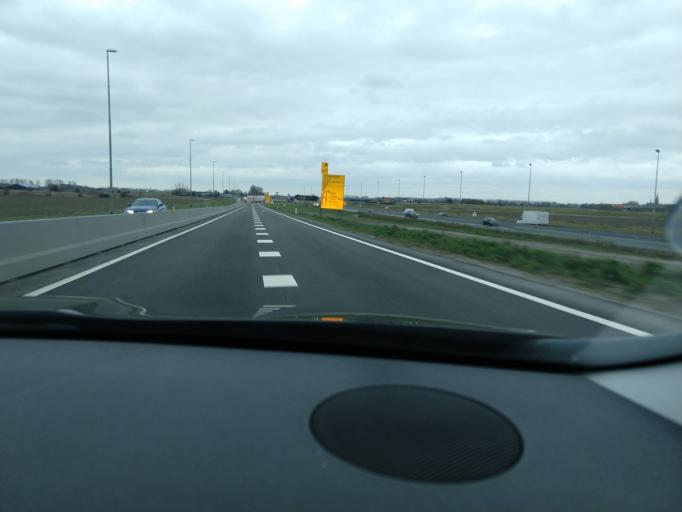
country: NL
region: Zeeland
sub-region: Gemeente Borsele
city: Borssele
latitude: 51.4597
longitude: 3.7481
